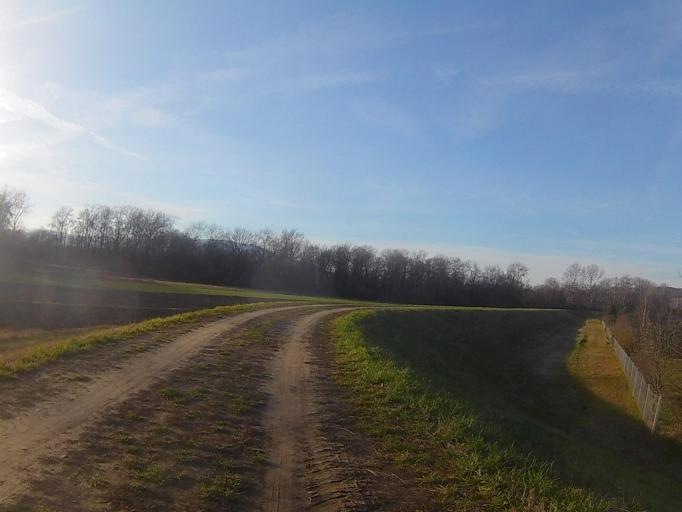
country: SI
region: Duplek
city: Spodnji Duplek
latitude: 46.5013
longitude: 15.7434
